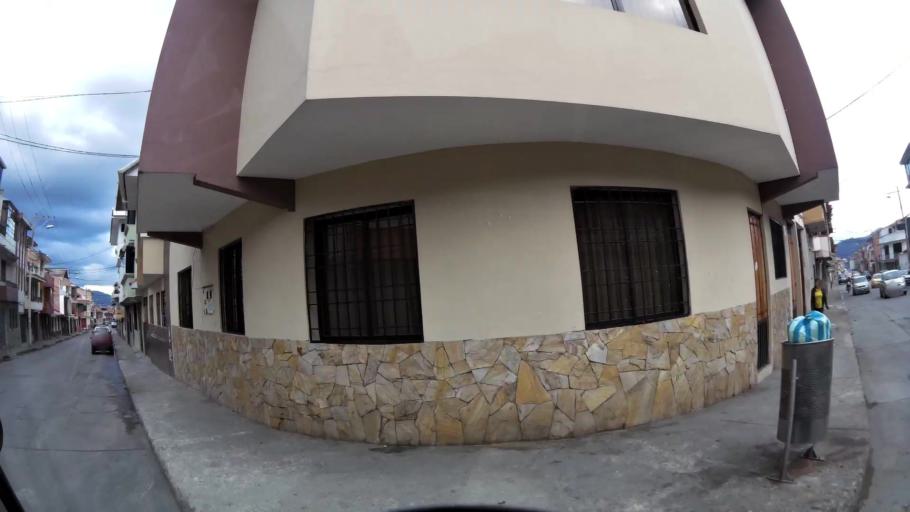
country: EC
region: Azuay
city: Cuenca
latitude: -2.8903
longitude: -79.0110
